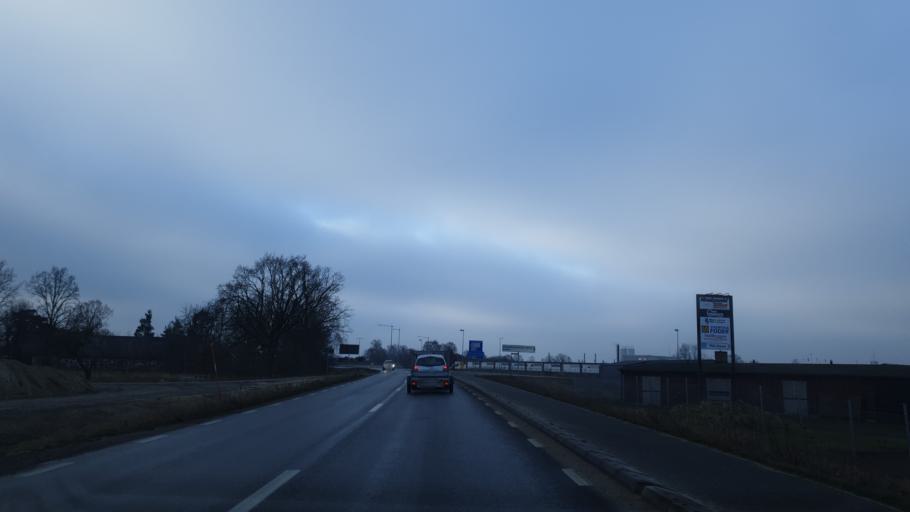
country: SE
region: Blekinge
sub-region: Solvesborgs Kommun
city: Soelvesborg
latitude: 56.0648
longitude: 14.6288
